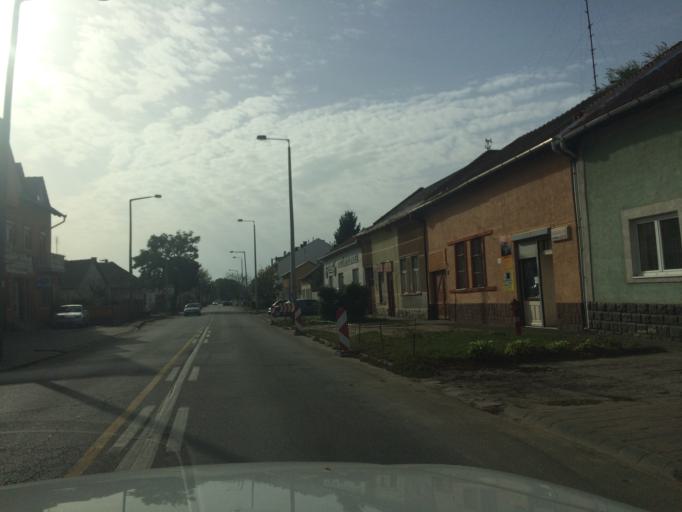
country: HU
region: Szabolcs-Szatmar-Bereg
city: Nyiregyhaza
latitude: 47.9462
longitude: 21.7190
